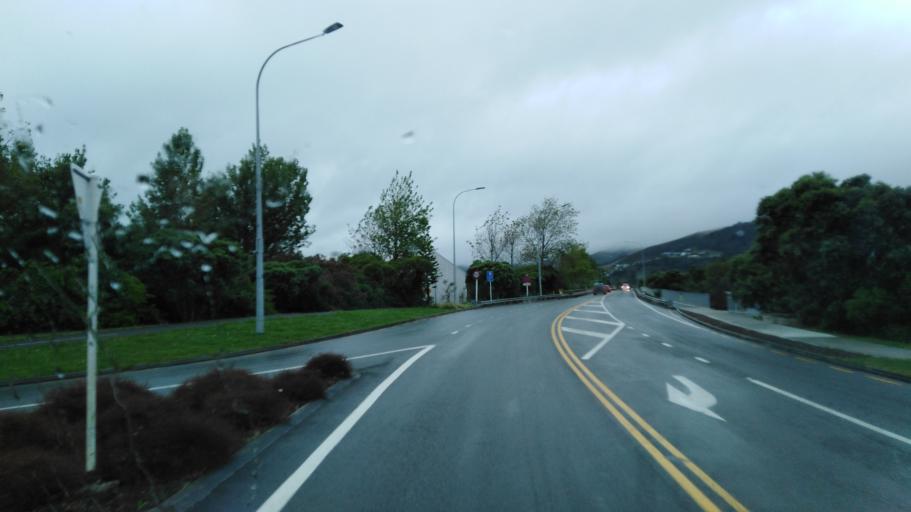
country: NZ
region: Nelson
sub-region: Nelson City
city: Nelson
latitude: -41.2663
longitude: 173.2791
